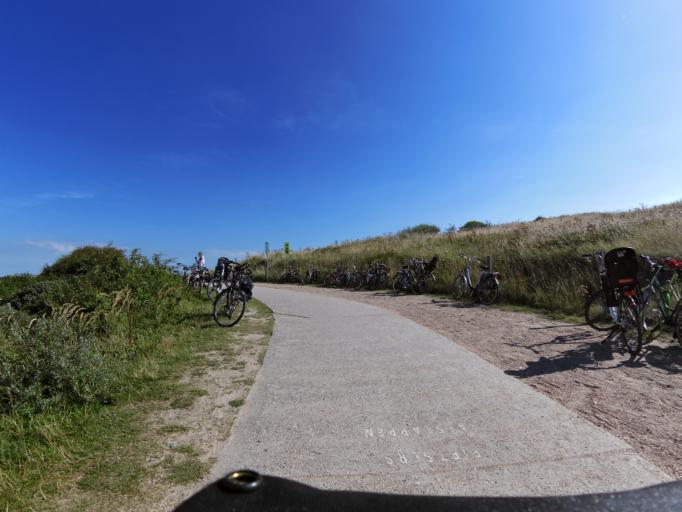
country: NL
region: Zeeland
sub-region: Schouwen-Duiveland
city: Haamstede
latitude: 51.7283
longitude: 3.7192
